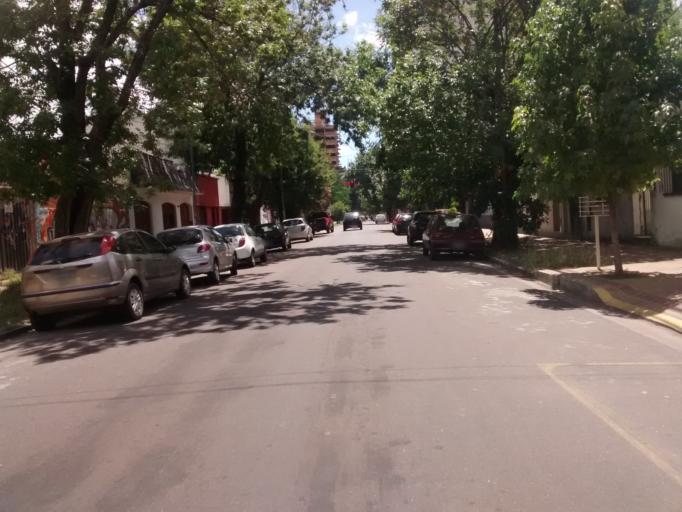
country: AR
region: Buenos Aires
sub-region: Partido de La Plata
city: La Plata
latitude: -34.9125
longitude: -57.9643
